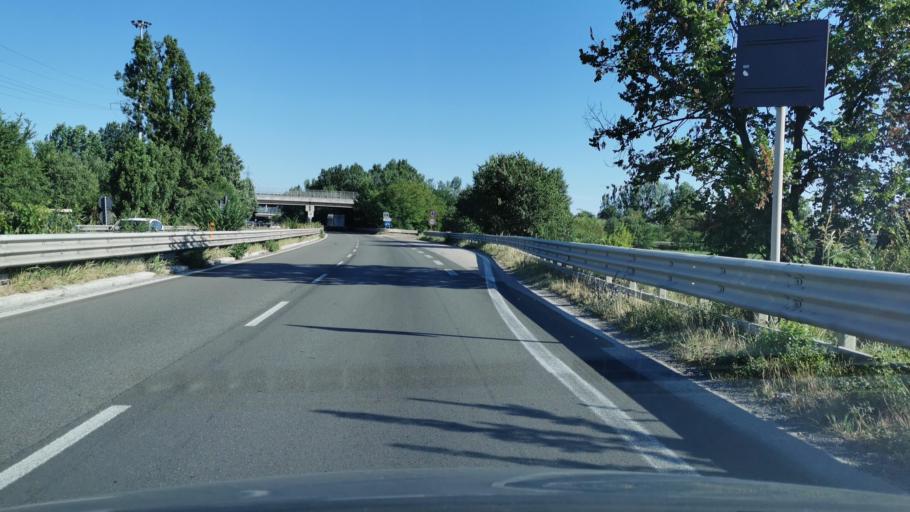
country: IT
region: Emilia-Romagna
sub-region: Provincia di Modena
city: Baggiovara
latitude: 44.6374
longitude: 10.8817
